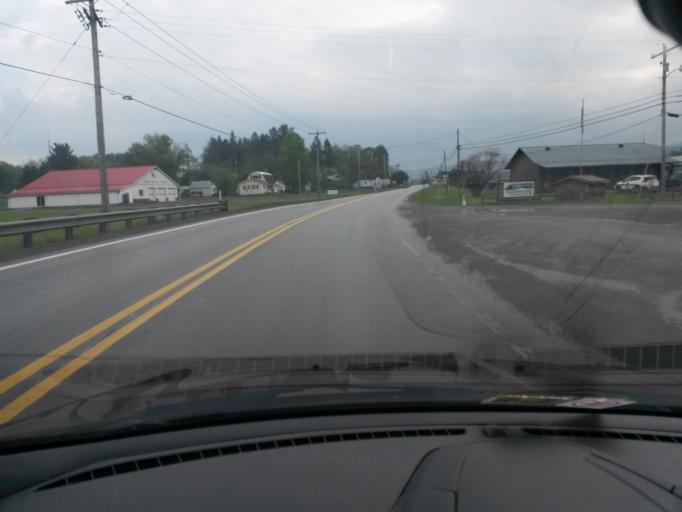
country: US
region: West Virginia
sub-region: Randolph County
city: Elkins
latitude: 38.7948
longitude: -79.9024
